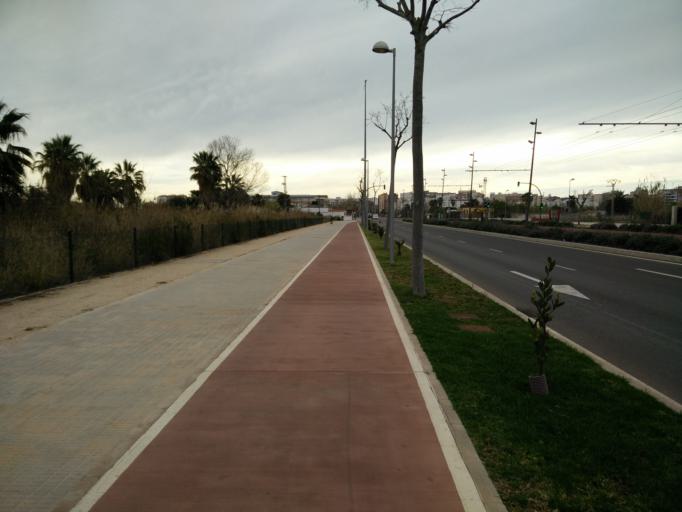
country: ES
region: Valencia
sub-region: Provincia de Castello
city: Castello de la Plana
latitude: 39.9781
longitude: 0.0042
